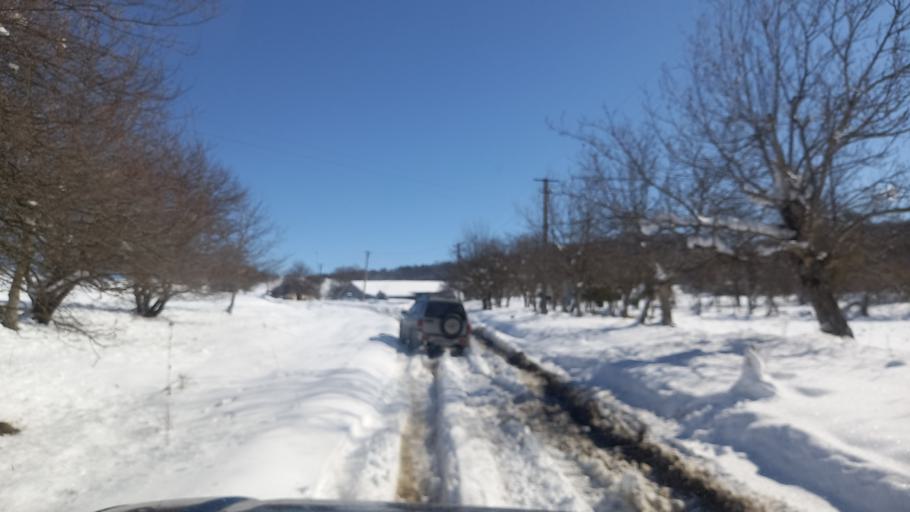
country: RU
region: Adygeya
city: Abadzekhskaya
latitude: 44.3389
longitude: 40.4135
